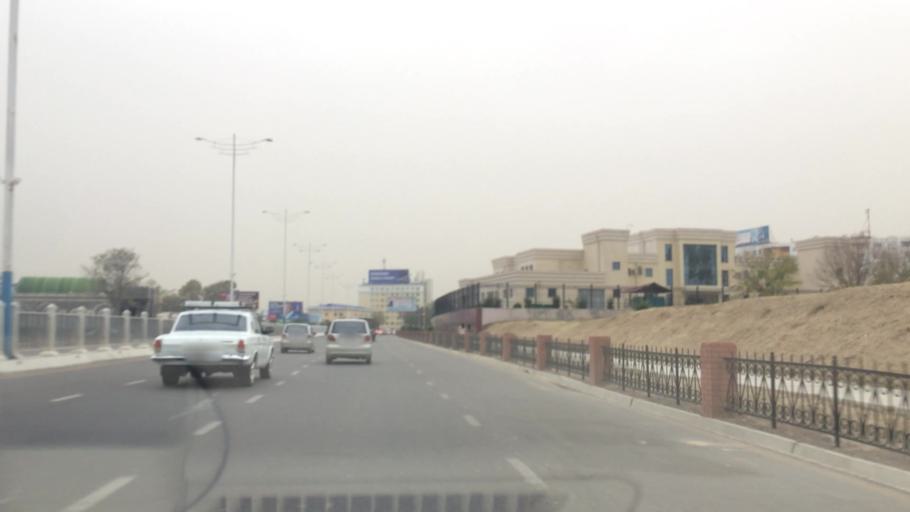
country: UZ
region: Toshkent Shahri
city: Bektemir
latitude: 41.3047
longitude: 69.3102
